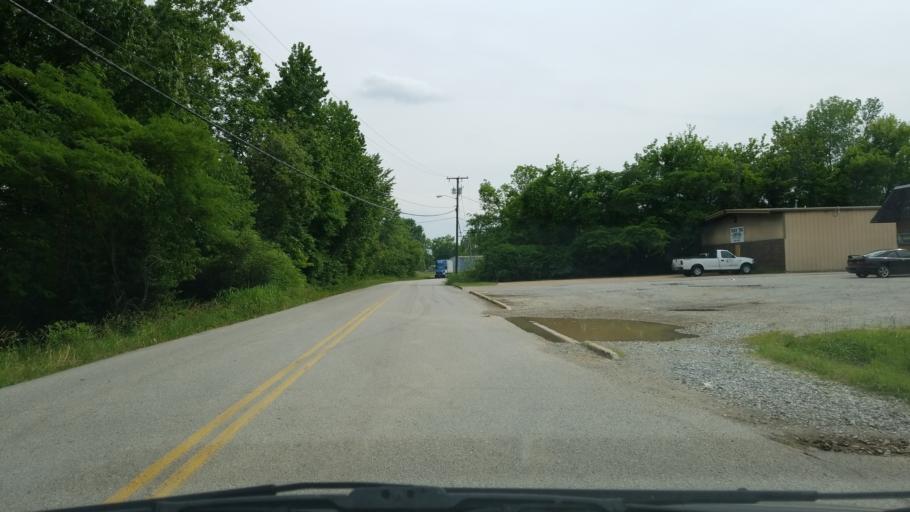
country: US
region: Tennessee
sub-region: Hamilton County
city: East Brainerd
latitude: 35.0429
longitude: -85.1878
